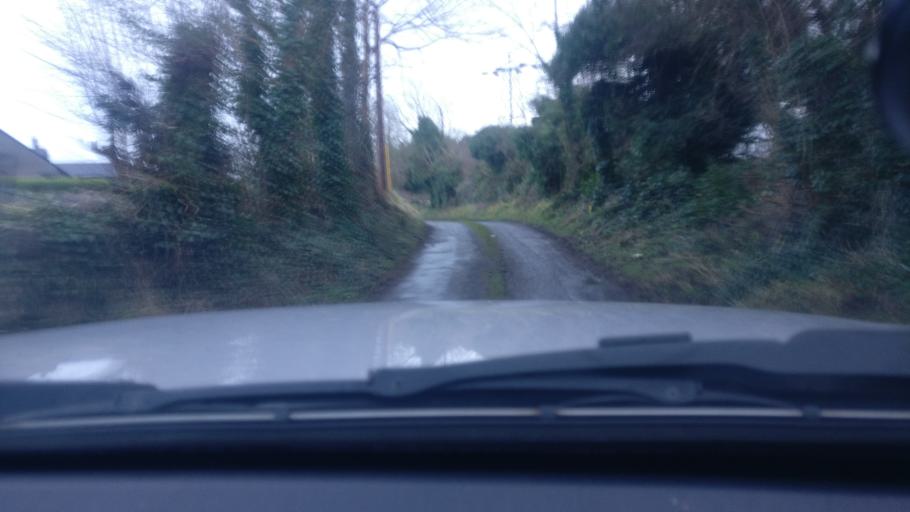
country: IE
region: Connaught
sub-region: County Galway
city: Loughrea
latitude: 53.1833
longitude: -8.6042
